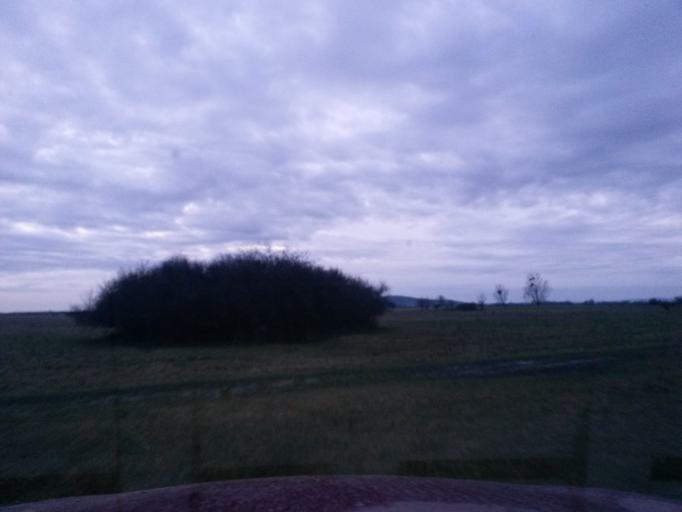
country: HU
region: Borsod-Abauj-Zemplen
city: Karcsa
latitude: 48.4174
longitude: 21.8744
